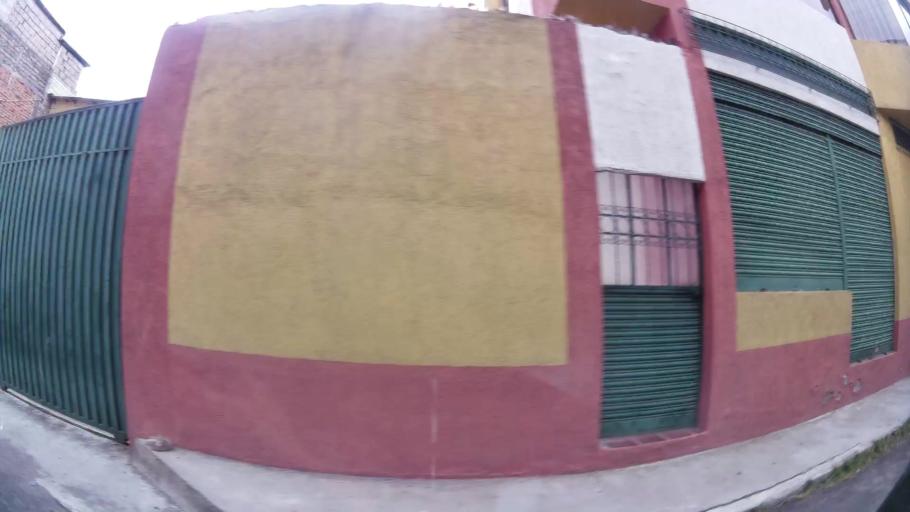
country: EC
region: Pichincha
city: Quito
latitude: -0.1917
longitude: -78.5085
